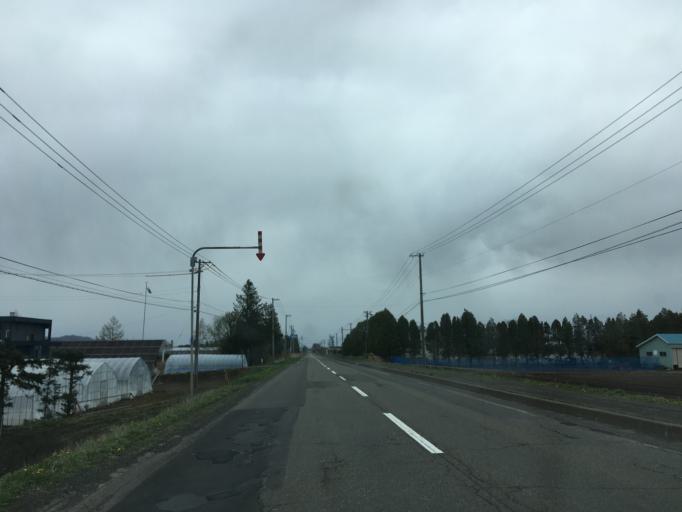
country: JP
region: Hokkaido
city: Chitose
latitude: 42.9306
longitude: 141.8069
